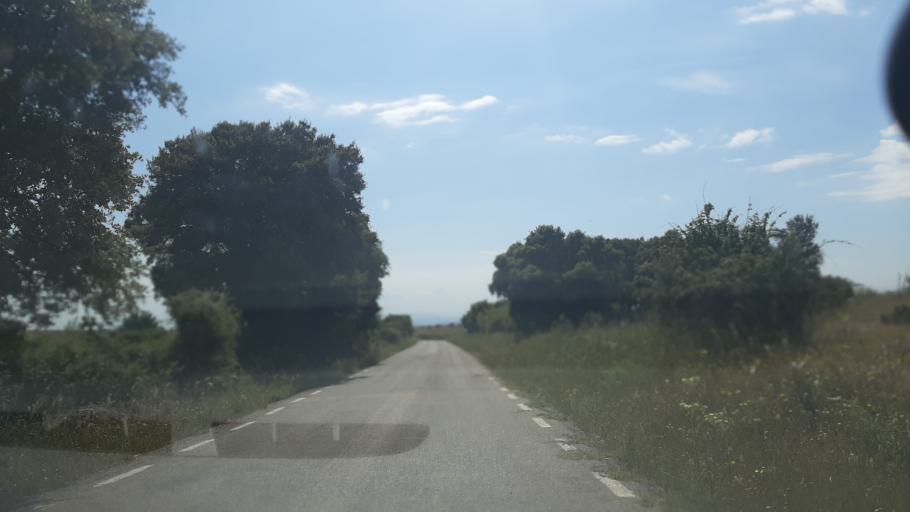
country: ES
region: Castille and Leon
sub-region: Provincia de Salamanca
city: Gallegos de Arganan
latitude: 40.6417
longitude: -6.7333
